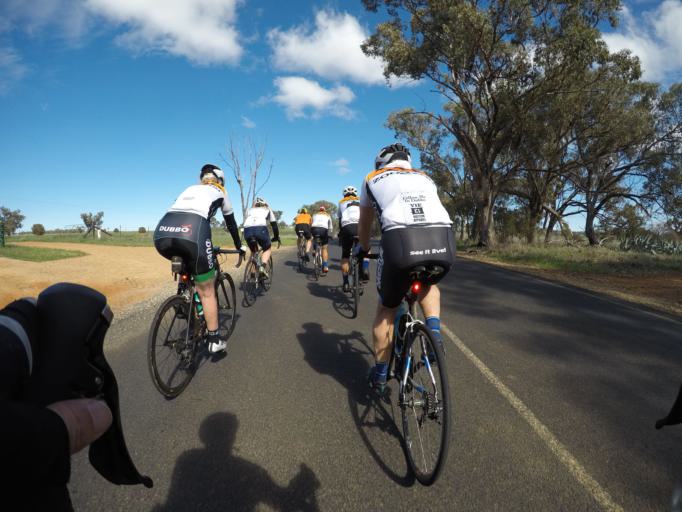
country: AU
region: New South Wales
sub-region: Wellington
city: Wellington
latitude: -32.7509
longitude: 148.6224
